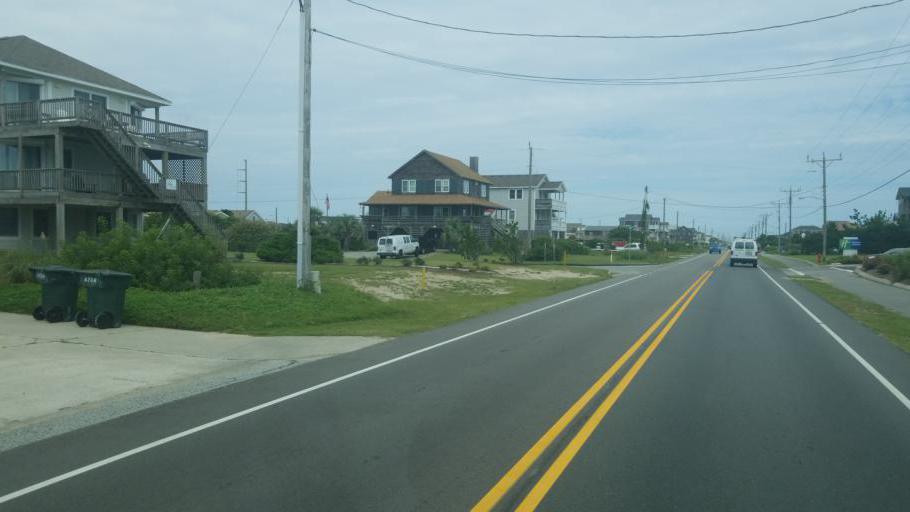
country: US
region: North Carolina
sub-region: Dare County
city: Nags Head
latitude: 35.9442
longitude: -75.6168
